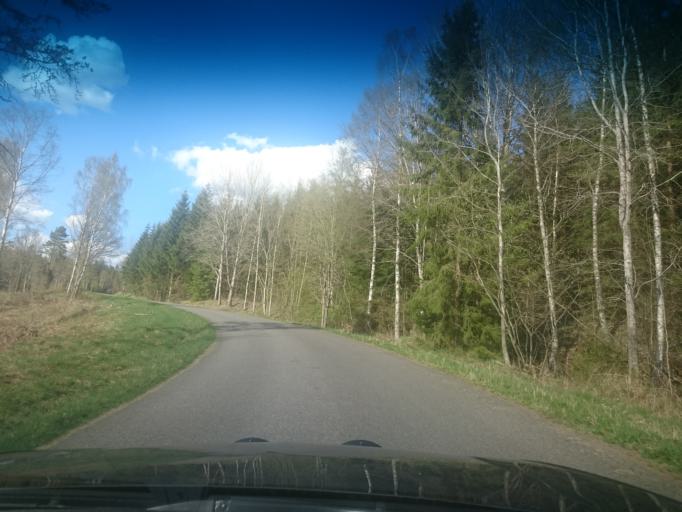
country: SE
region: Kronoberg
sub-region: Vaxjo Kommun
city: Braas
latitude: 57.1465
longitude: 15.1605
